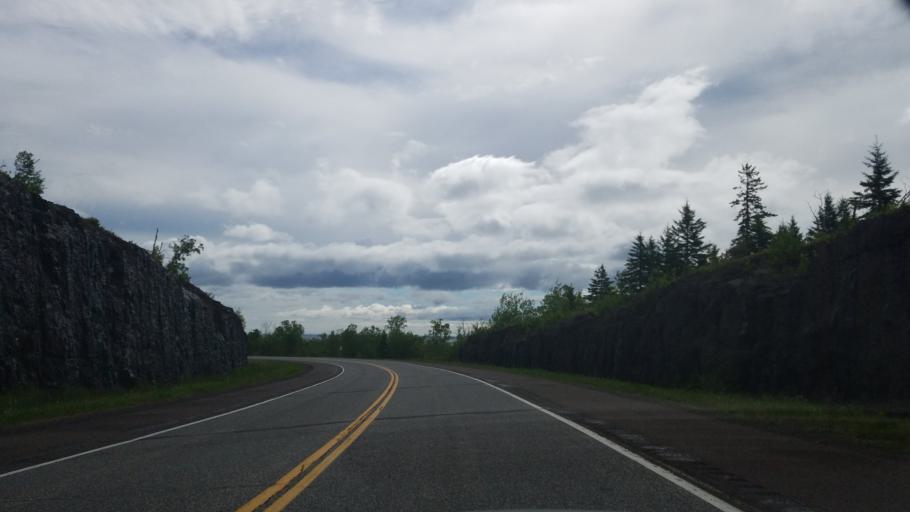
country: US
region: Minnesota
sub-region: Lake County
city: Two Harbors
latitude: 47.1466
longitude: -91.4565
